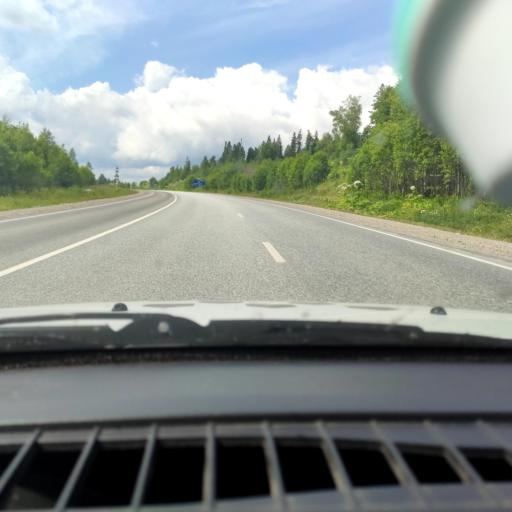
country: RU
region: Perm
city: Polazna
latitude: 58.2925
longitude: 56.4887
